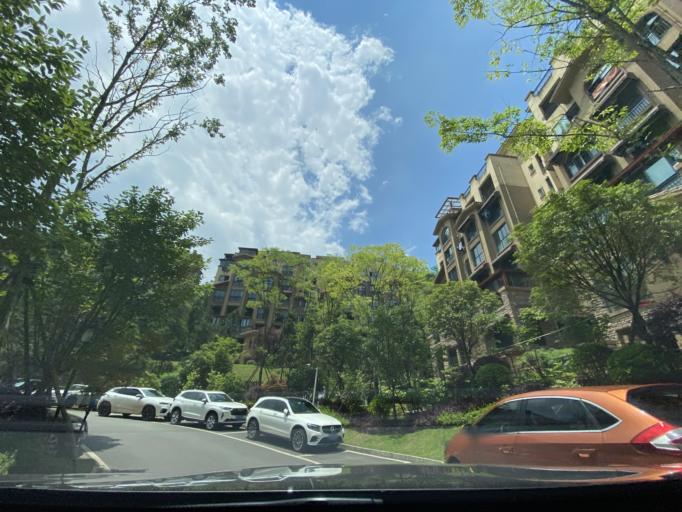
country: CN
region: Guizhou Sheng
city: Changqi
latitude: 28.5382
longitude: 105.9790
